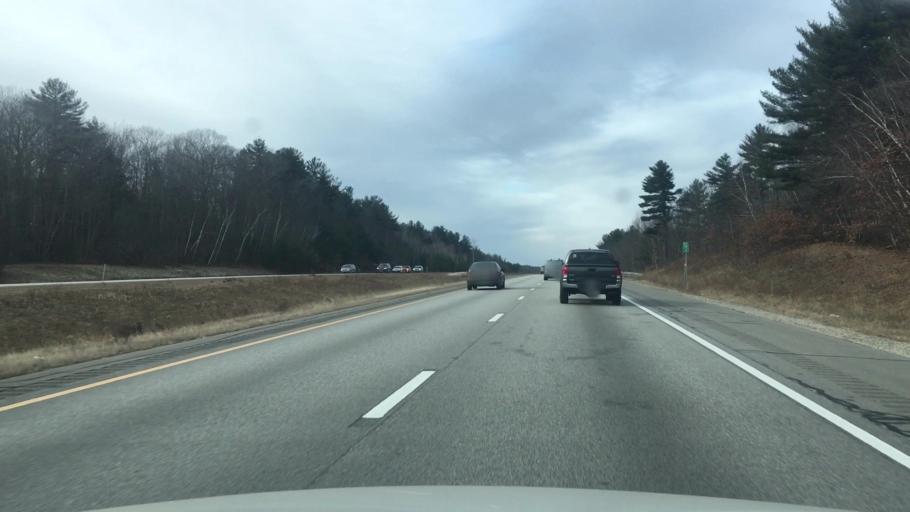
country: US
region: New Hampshire
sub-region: Rockingham County
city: Raymond
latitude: 43.0245
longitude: -71.2345
